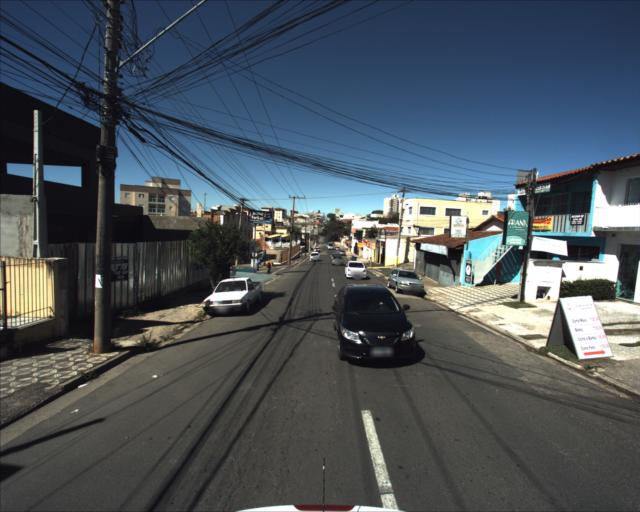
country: BR
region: Sao Paulo
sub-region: Sorocaba
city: Sorocaba
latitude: -23.5049
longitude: -47.4928
